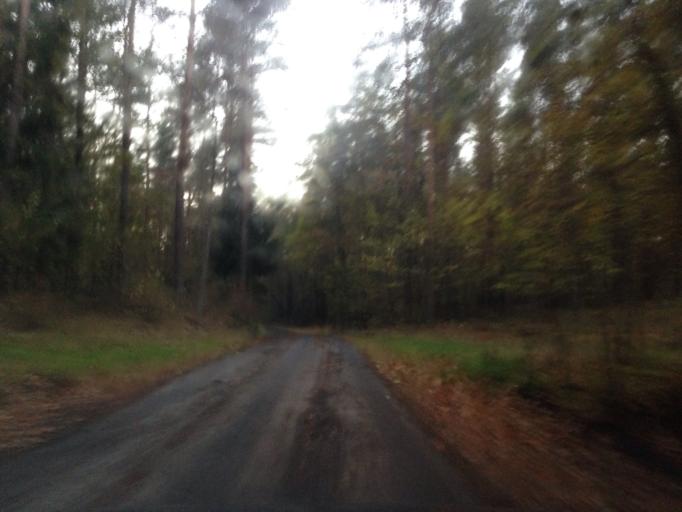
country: PL
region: Kujawsko-Pomorskie
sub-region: Powiat brodnicki
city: Gorzno
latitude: 53.2242
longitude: 19.6988
